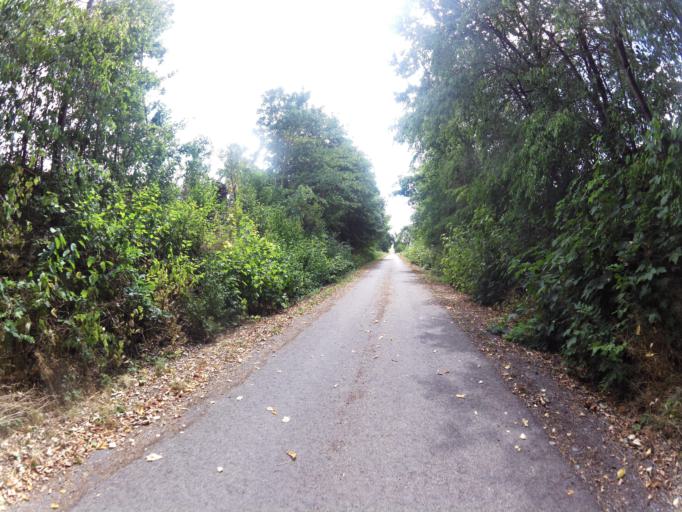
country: DE
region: Bavaria
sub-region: Regierungsbezirk Unterfranken
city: Aub
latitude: 49.5449
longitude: 10.0426
